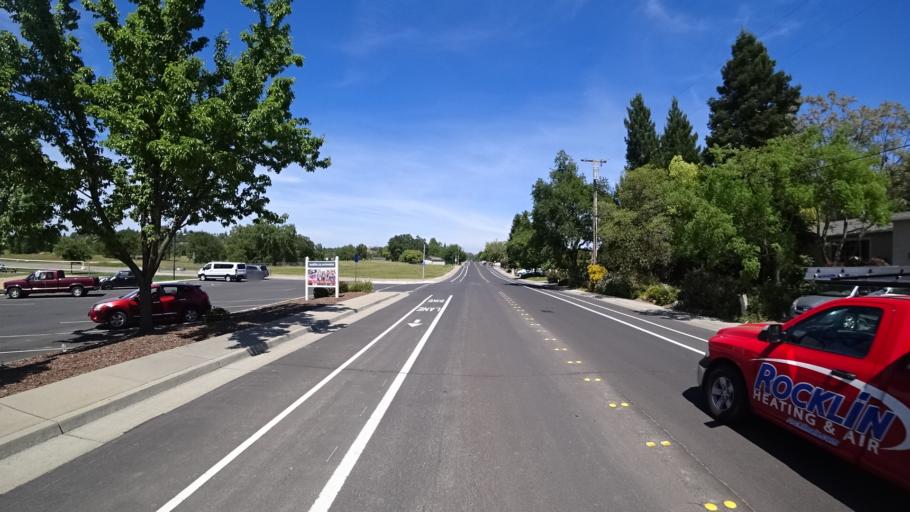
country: US
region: California
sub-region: Placer County
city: Rocklin
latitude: 38.7906
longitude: -121.2433
